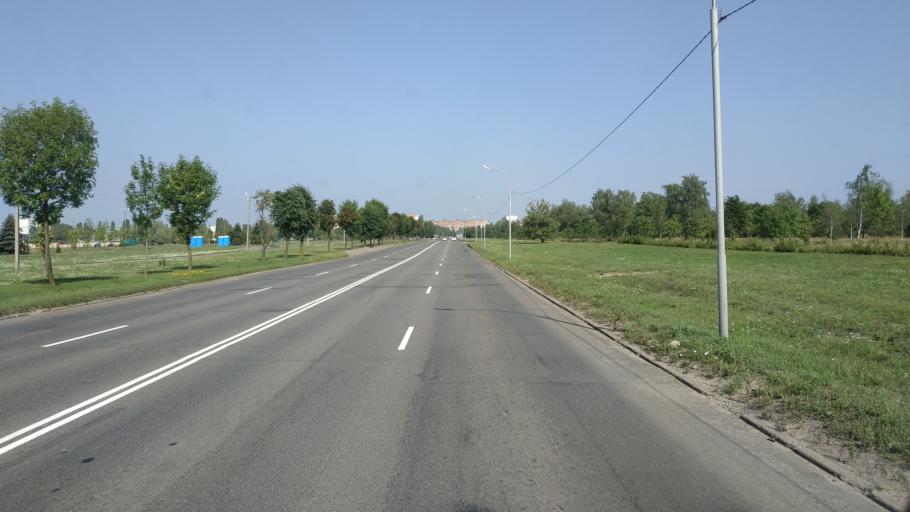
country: BY
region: Mogilev
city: Buynichy
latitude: 53.8611
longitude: 30.3234
